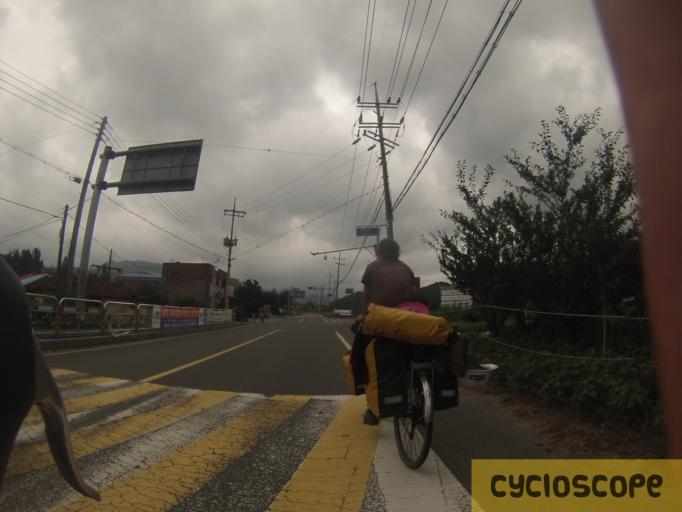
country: KR
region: Chungcheongnam-do
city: Hongsung
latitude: 36.5322
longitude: 126.7705
